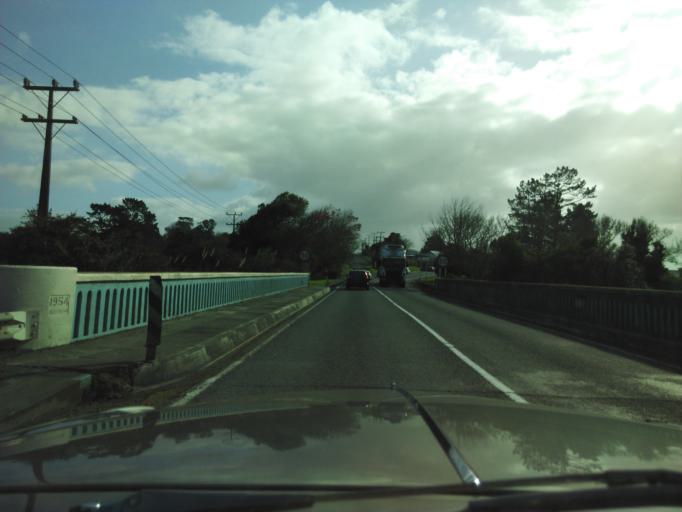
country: NZ
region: Auckland
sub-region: Auckland
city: Wellsford
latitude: -36.3034
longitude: 174.5267
